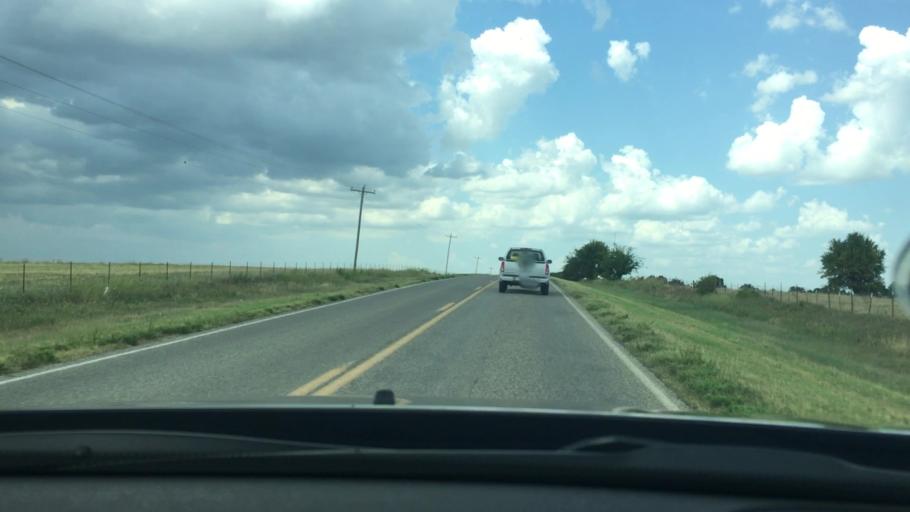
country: US
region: Oklahoma
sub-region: Pontotoc County
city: Ada
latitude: 34.5517
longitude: -96.6347
